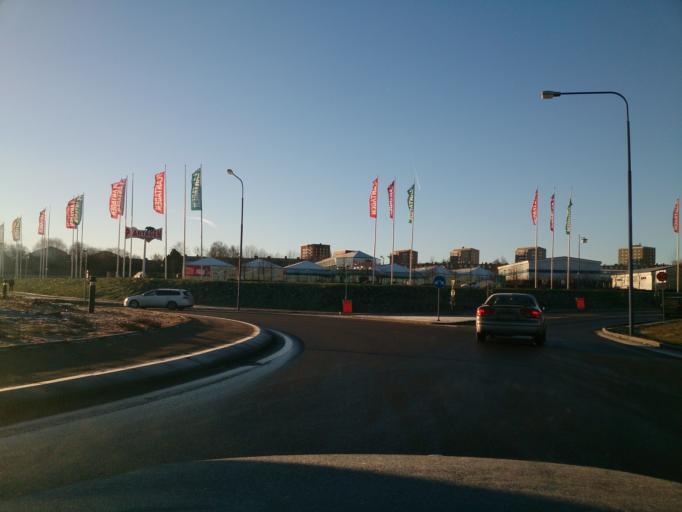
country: SE
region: OEstergoetland
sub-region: Norrkopings Kommun
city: Norrkoping
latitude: 58.6117
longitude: 16.1600
